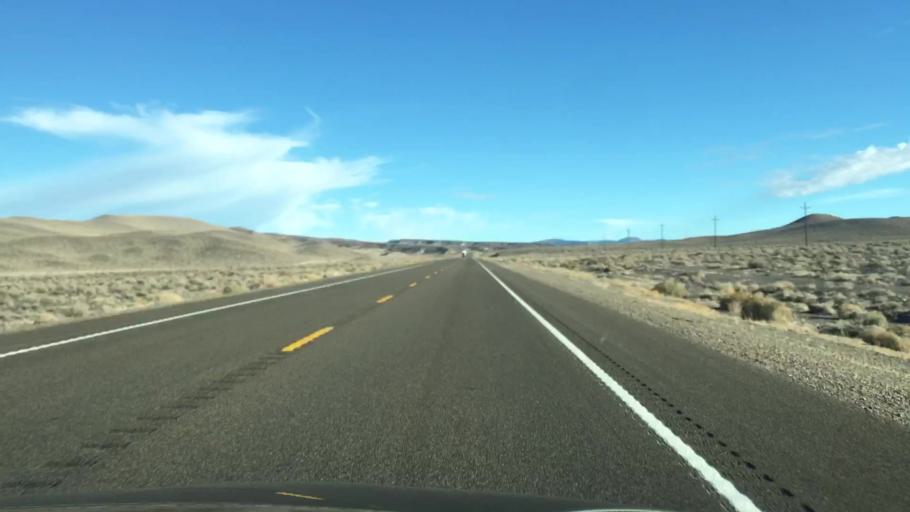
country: US
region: Nevada
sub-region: Mineral County
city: Hawthorne
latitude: 38.2401
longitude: -118.0391
